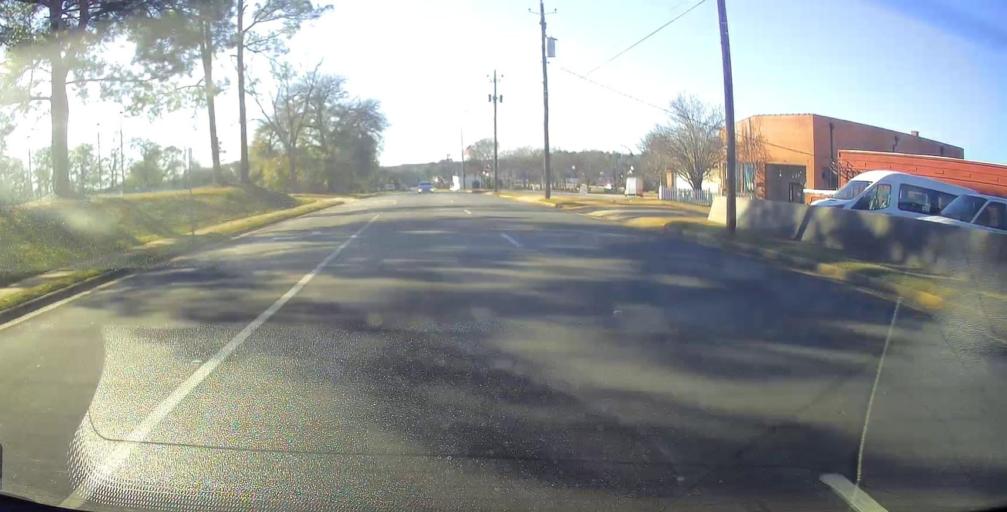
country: US
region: Georgia
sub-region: Sumter County
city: Americus
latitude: 32.0724
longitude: -84.2382
